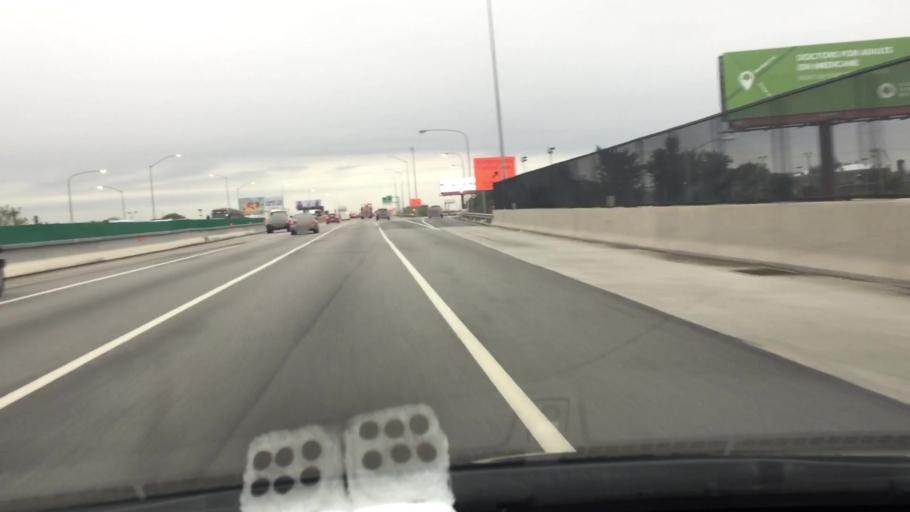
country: US
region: New Jersey
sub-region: Camden County
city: Merchantville
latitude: 39.9814
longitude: -75.1019
